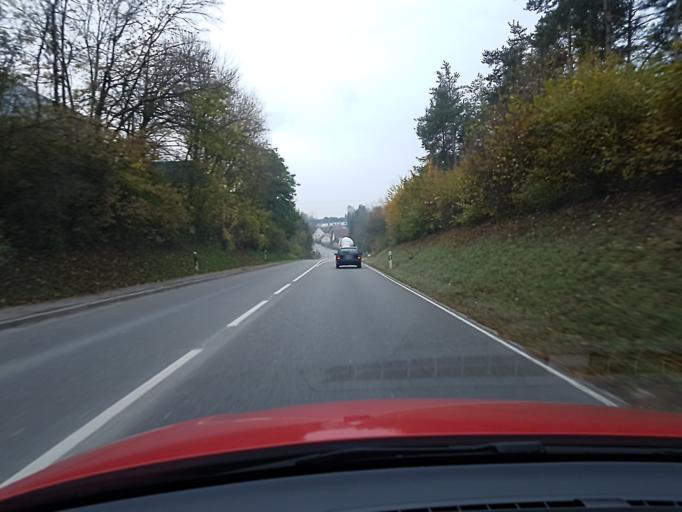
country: DE
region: Baden-Wuerttemberg
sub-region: Regierungsbezirk Stuttgart
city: Talheim
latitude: 49.0985
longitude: 9.1843
